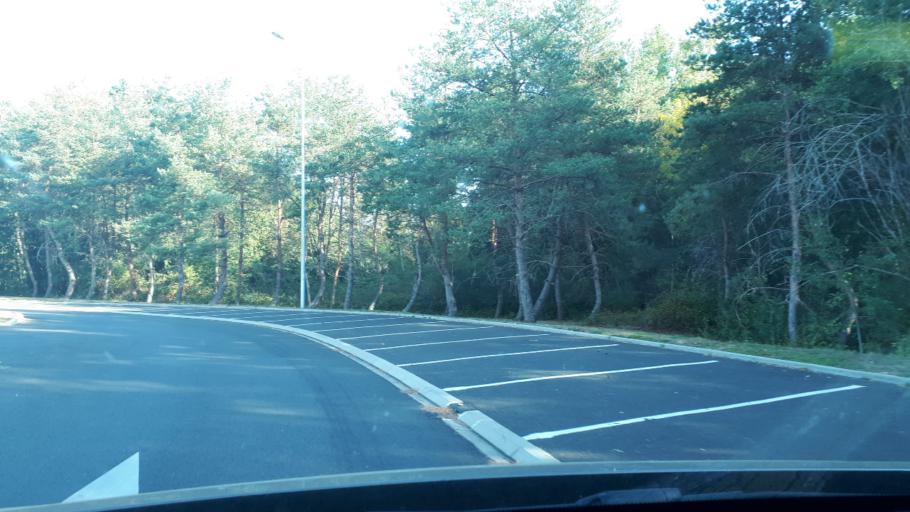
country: FR
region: Centre
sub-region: Departement du Loir-et-Cher
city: Naveil
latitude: 47.8224
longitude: 1.0227
